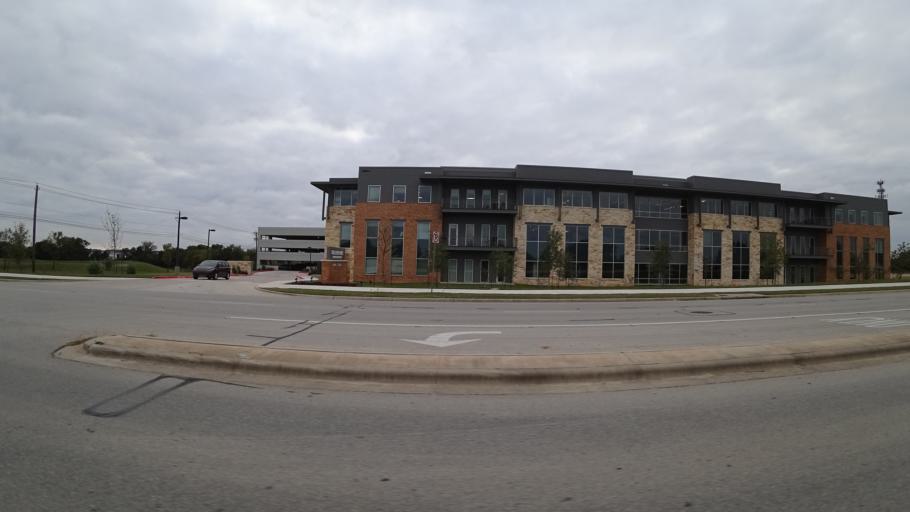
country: US
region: Texas
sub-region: Travis County
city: Bee Cave
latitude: 30.3142
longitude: -97.9451
